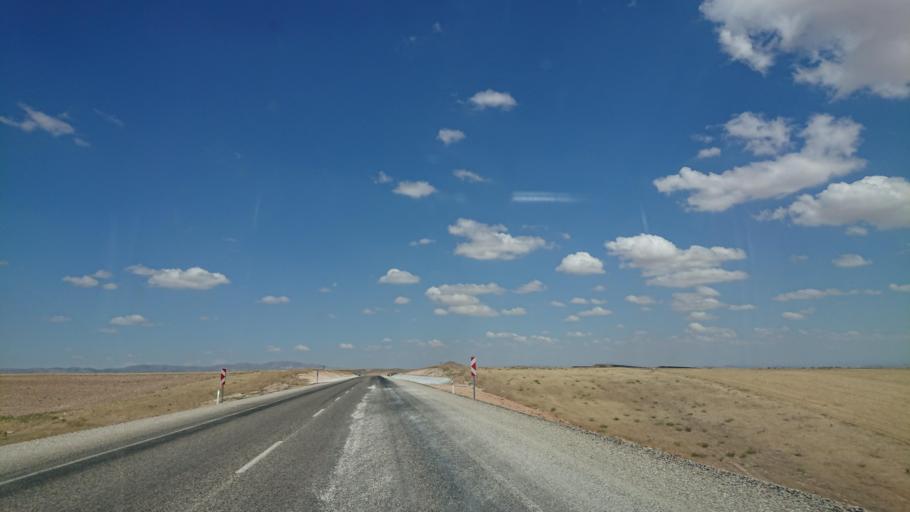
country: TR
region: Kirsehir
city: Kirsehir
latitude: 39.1229
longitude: 34.0002
